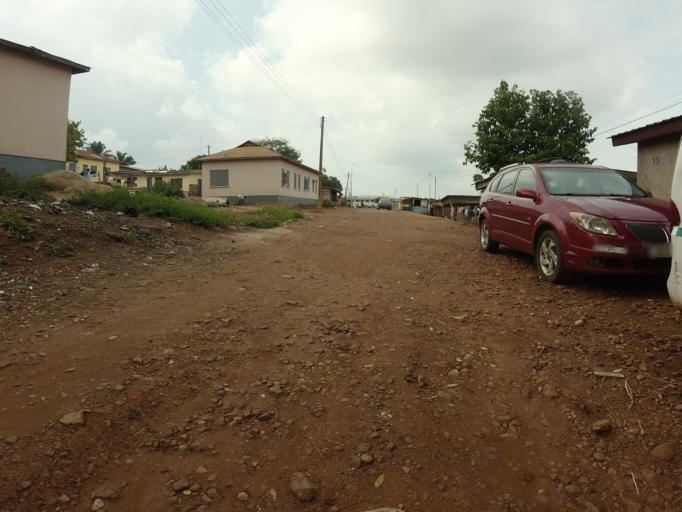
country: GH
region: Volta
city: Ho
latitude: 6.6175
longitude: 0.4648
